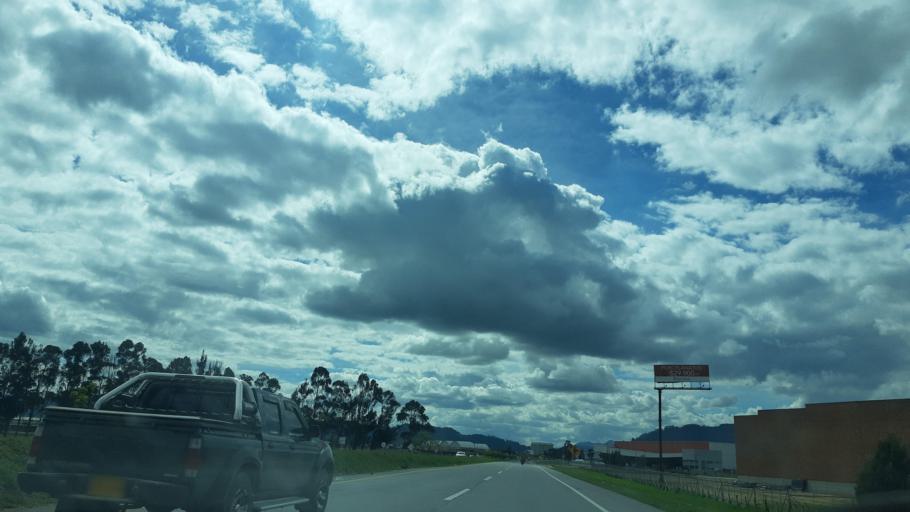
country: CO
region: Cundinamarca
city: Tocancipa
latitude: 4.9549
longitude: -73.9248
